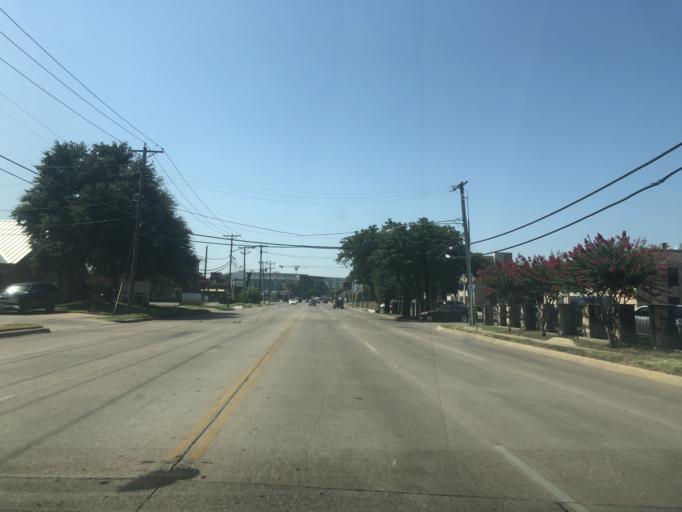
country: US
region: Texas
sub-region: Tarrant County
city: River Oaks
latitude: 32.7557
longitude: -97.3612
